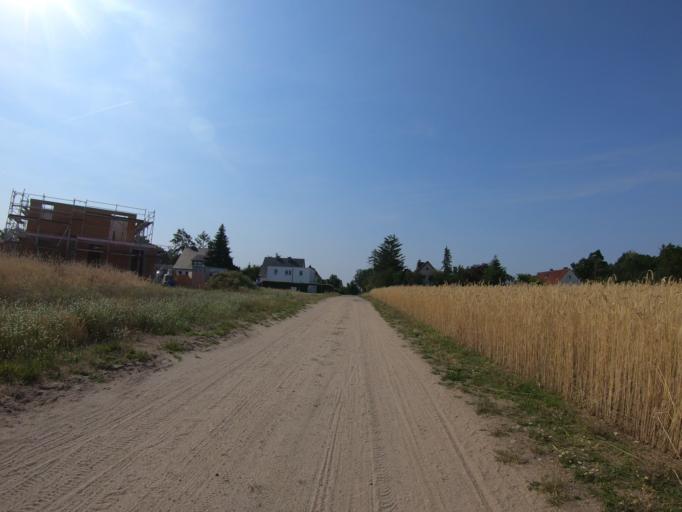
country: DE
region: Lower Saxony
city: Gifhorn
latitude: 52.4888
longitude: 10.5302
